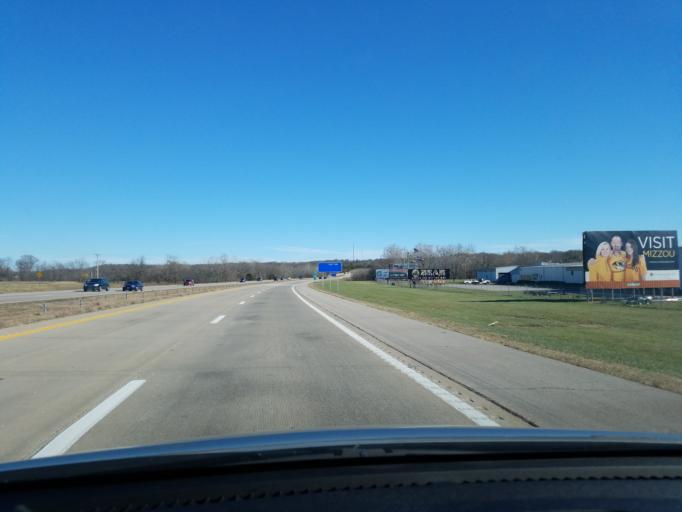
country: US
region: Missouri
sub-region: Pulaski County
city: Richland
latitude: 37.7607
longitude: -92.5255
